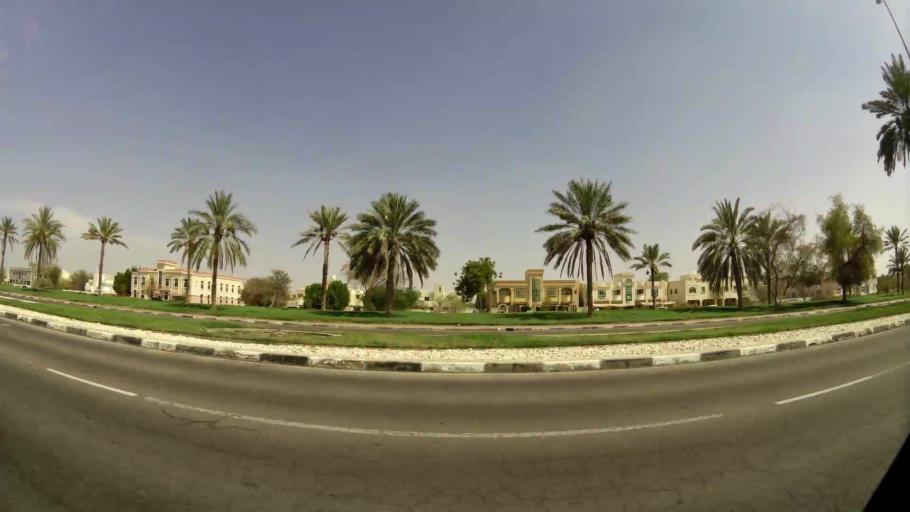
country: AE
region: Abu Dhabi
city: Al Ain
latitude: 24.2210
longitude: 55.6941
